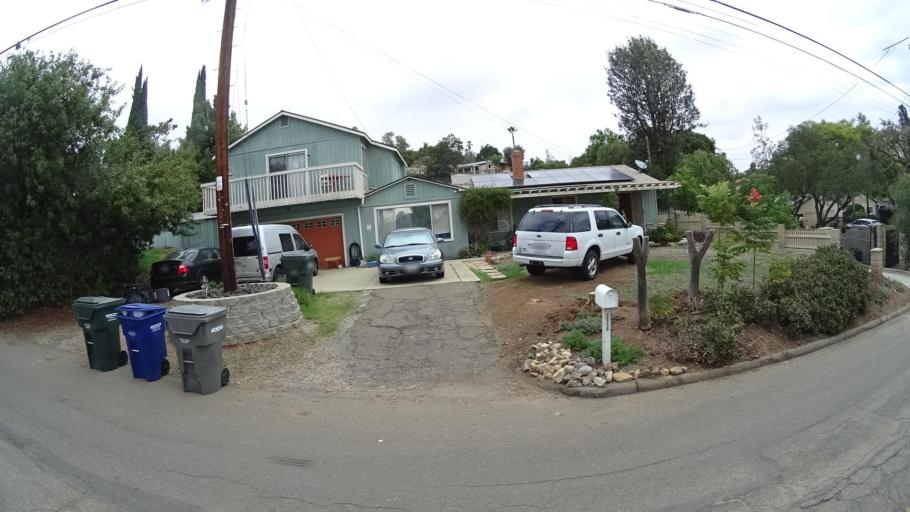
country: US
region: California
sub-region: San Diego County
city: Spring Valley
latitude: 32.7517
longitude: -116.9909
